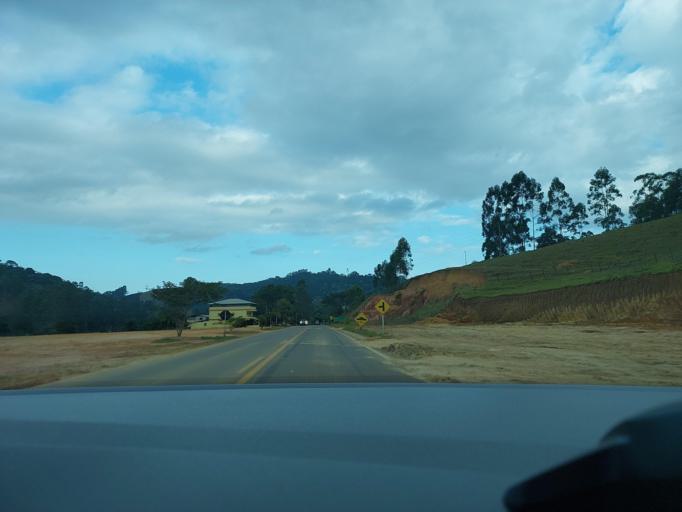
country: BR
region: Minas Gerais
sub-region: Mirai
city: Mirai
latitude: -20.9961
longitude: -42.5574
